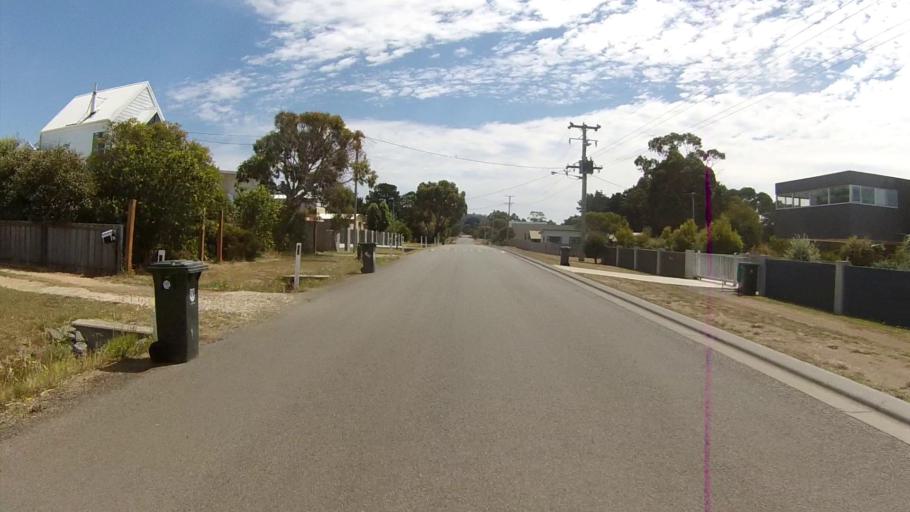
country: AU
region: Tasmania
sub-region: Clarence
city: Sandford
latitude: -42.9899
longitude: 147.5220
